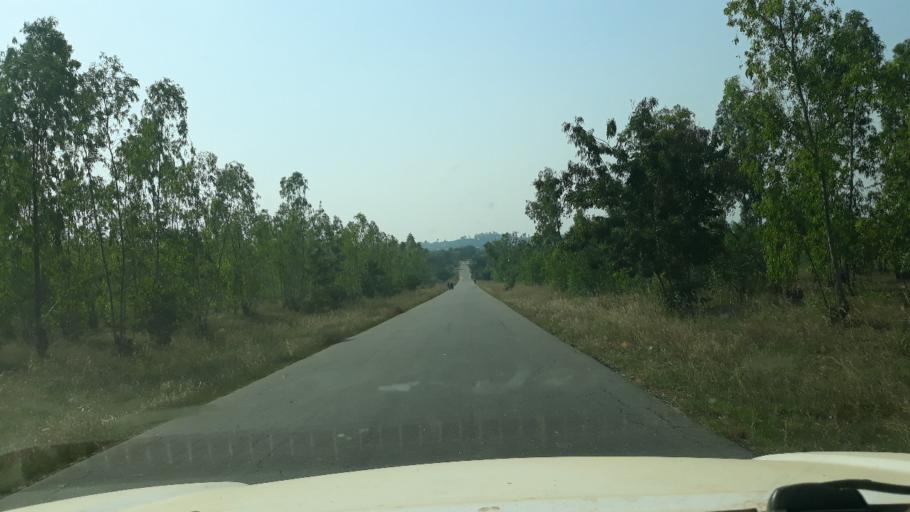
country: CD
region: South Kivu
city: Uvira
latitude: -3.1915
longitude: 29.1537
